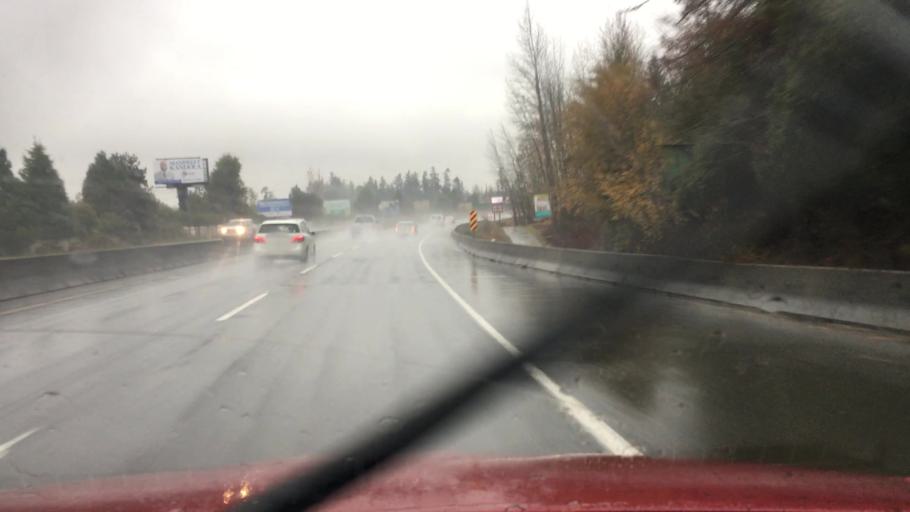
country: CA
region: British Columbia
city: North Saanich
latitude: 48.5865
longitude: -123.4013
